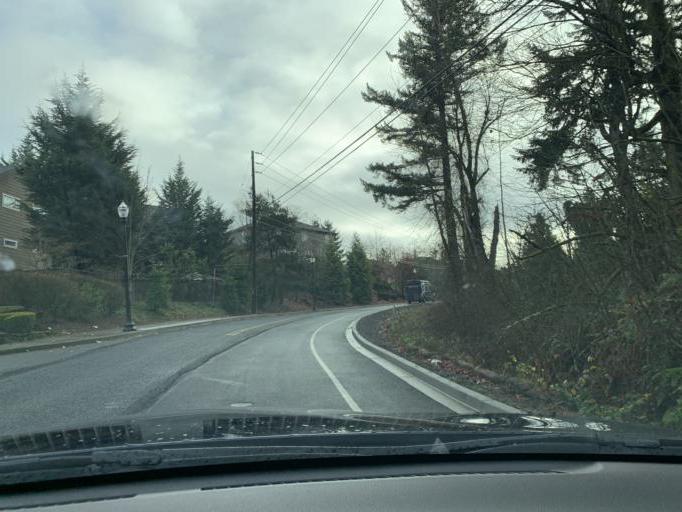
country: US
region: Oregon
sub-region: Multnomah County
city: Fairview
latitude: 45.5863
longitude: -122.4571
